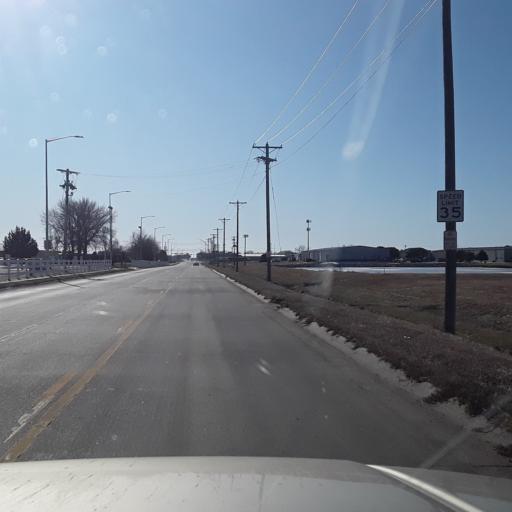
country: US
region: Nebraska
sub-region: Adams County
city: Hastings
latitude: 40.5729
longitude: -98.4021
